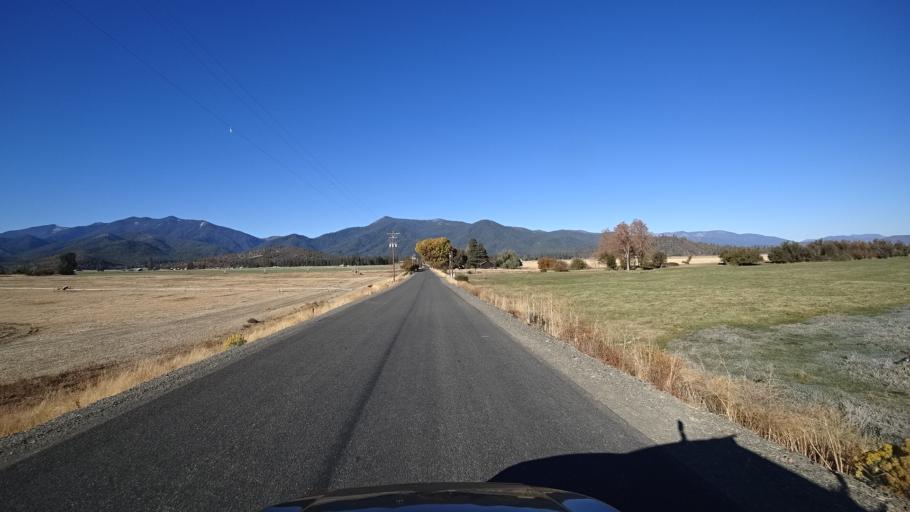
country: US
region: California
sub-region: Siskiyou County
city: Yreka
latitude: 41.4576
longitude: -122.8532
